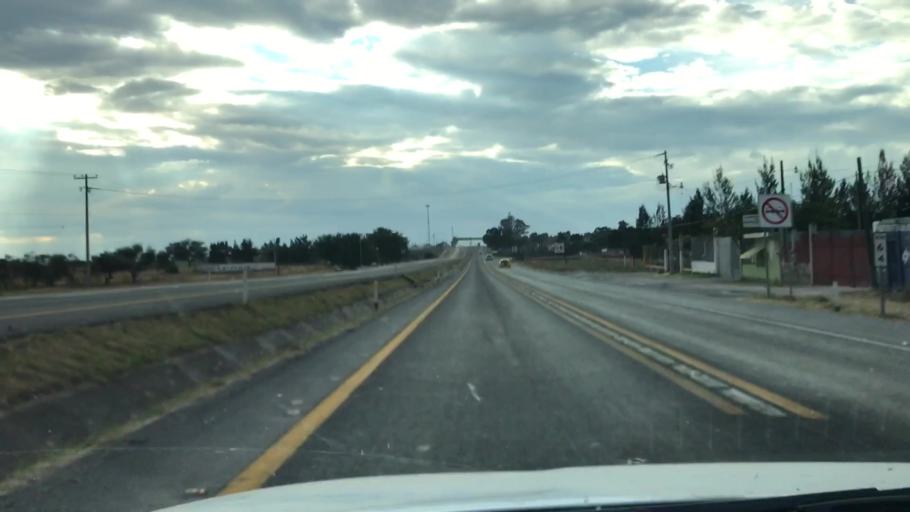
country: MX
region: Guanajuato
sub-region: Penjamo
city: Mezquite de Luna
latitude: 20.3804
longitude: -101.8269
